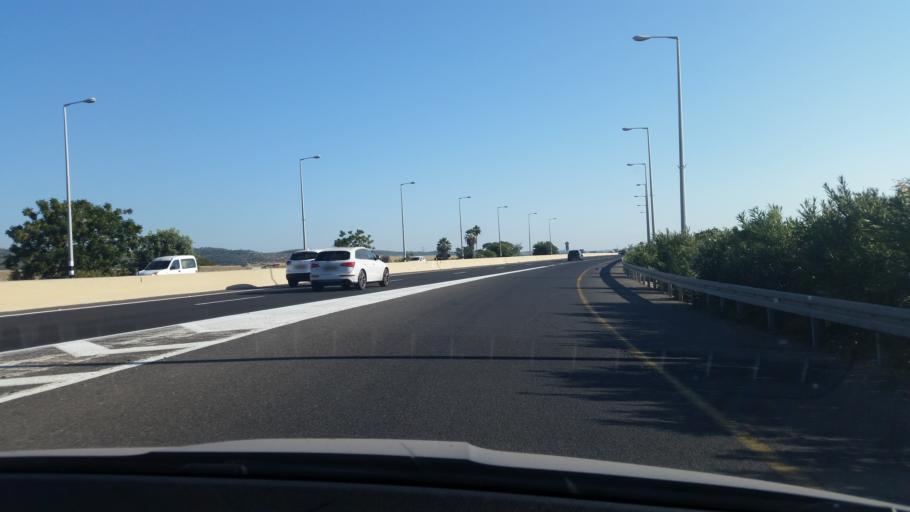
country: IL
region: Haifa
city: `Atlit
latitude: 32.7075
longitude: 34.9521
